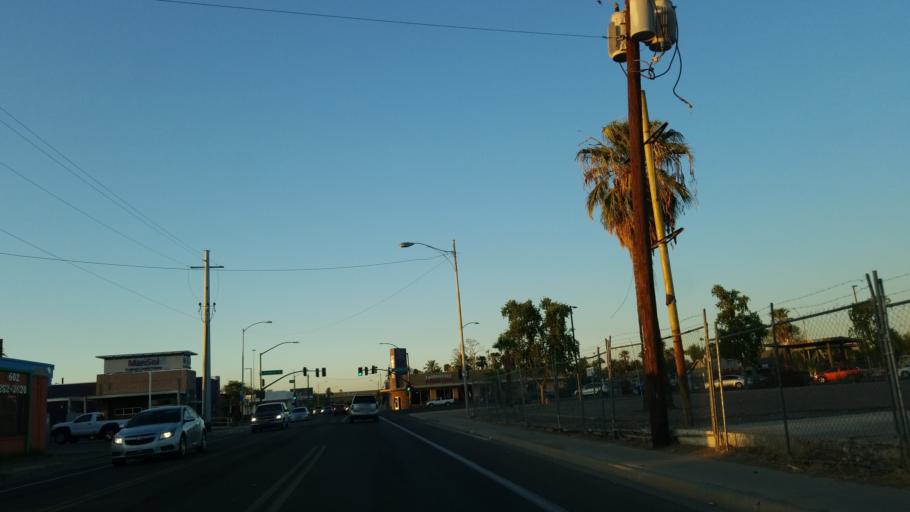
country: US
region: Arizona
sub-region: Maricopa County
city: Phoenix
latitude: 33.4584
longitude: -112.0919
